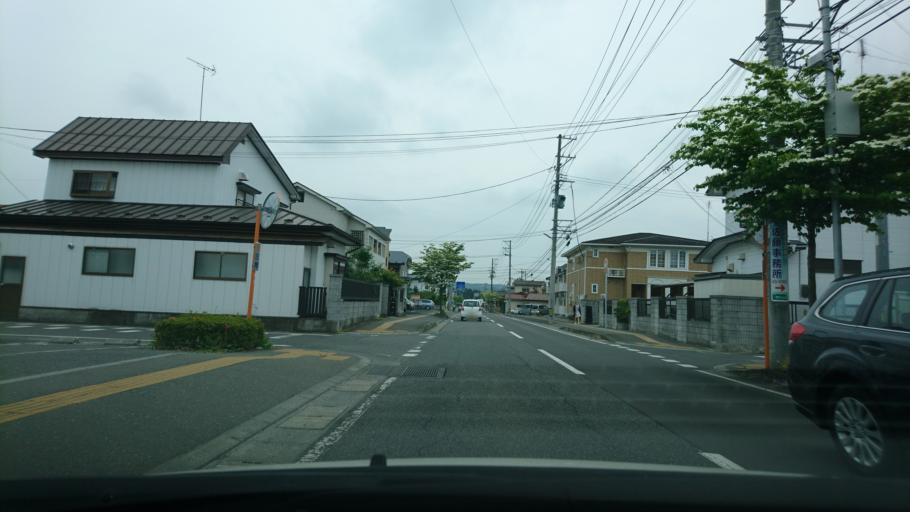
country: JP
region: Iwate
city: Ichinoseki
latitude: 38.9349
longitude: 141.1134
